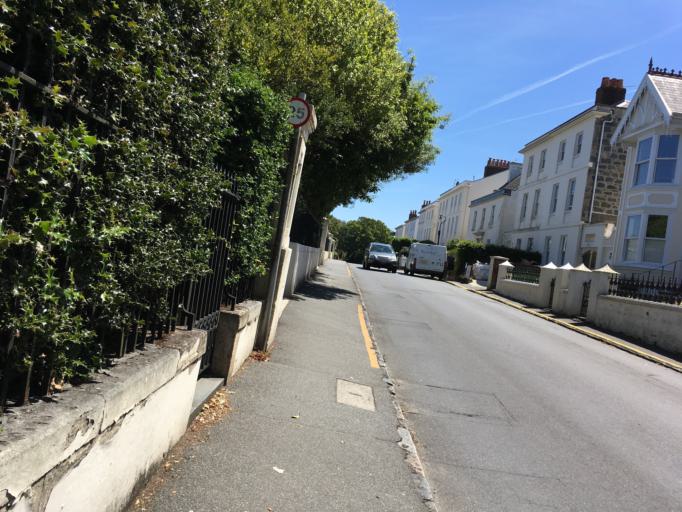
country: GG
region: St Peter Port
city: Saint Peter Port
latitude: 49.4597
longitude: -2.5439
